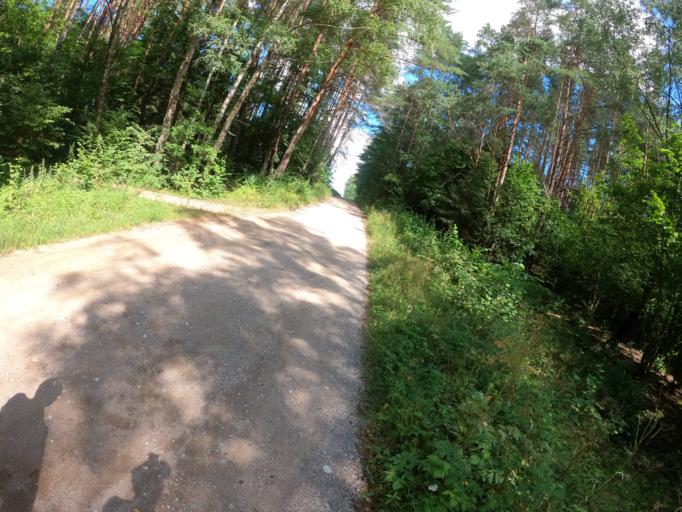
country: LT
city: Birstonas
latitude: 54.6212
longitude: 24.0314
